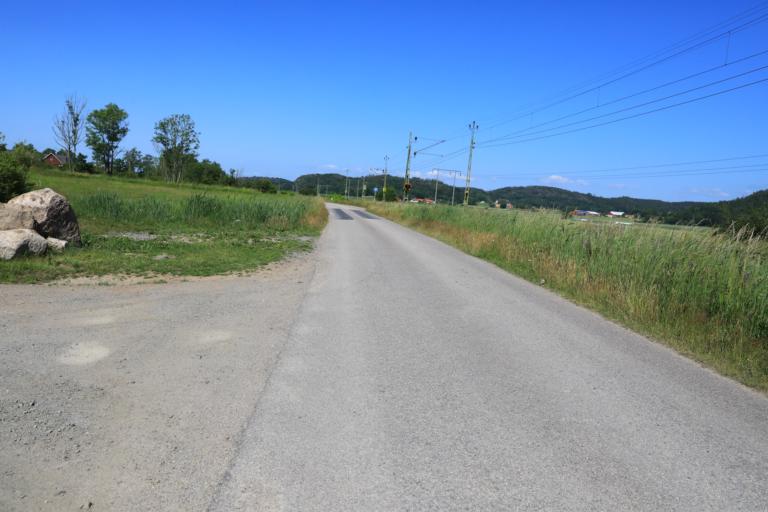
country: SE
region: Halland
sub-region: Varbergs Kommun
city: Varberg
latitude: 57.1770
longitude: 12.3026
